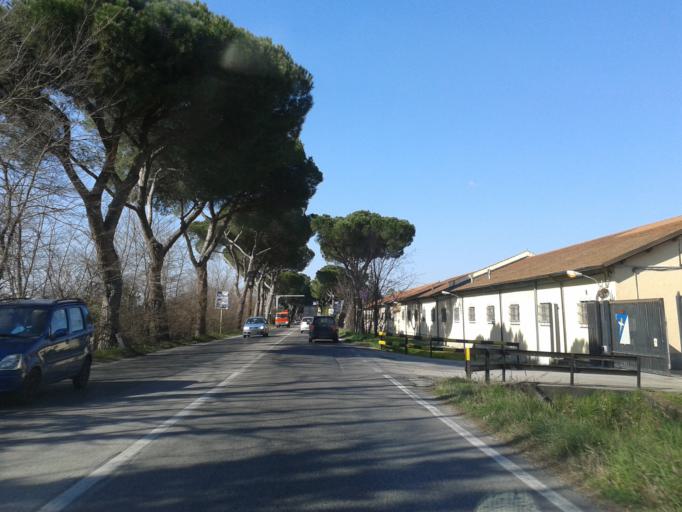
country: IT
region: Tuscany
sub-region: Province of Pisa
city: Pisa
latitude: 43.7130
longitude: 10.3838
